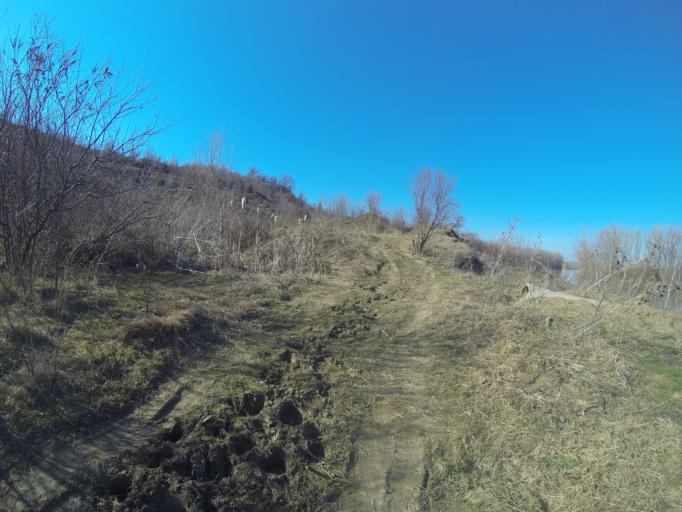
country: RO
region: Dolj
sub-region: Comuna Teascu
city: Teasc
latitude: 44.1517
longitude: 23.8340
